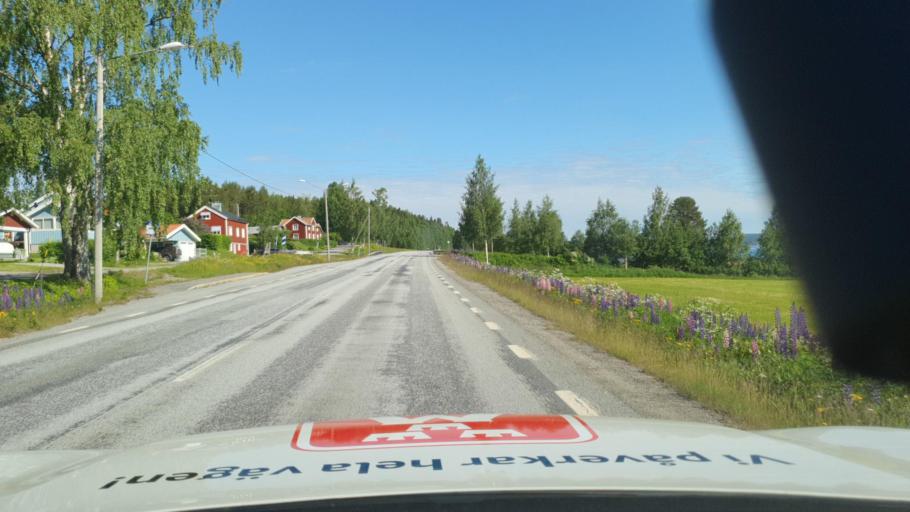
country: SE
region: Vaesterbotten
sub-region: Vannas Kommun
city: Vannasby
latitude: 63.9972
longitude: 20.0361
